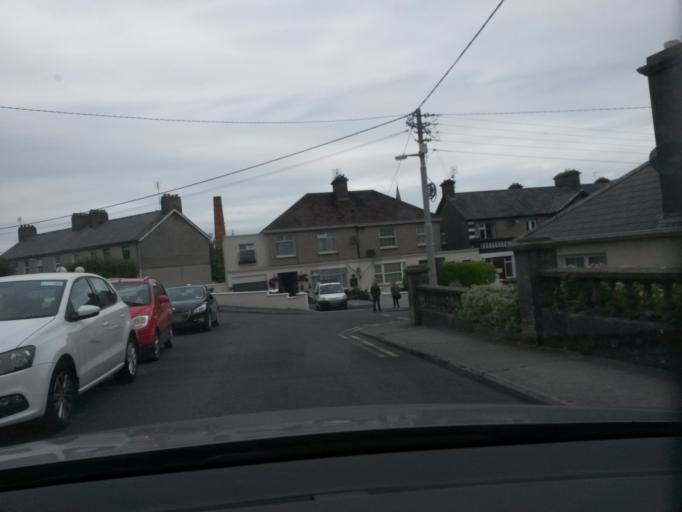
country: IE
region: Munster
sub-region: An Clar
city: Ennis
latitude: 52.8397
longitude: -8.9791
